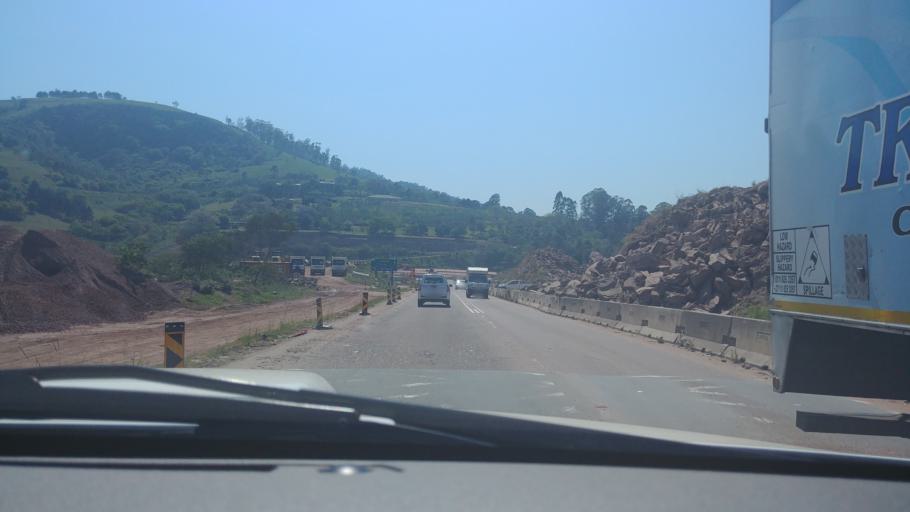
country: ZA
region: KwaZulu-Natal
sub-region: eThekwini Metropolitan Municipality
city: Mpumalanga
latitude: -29.7591
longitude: 30.6638
